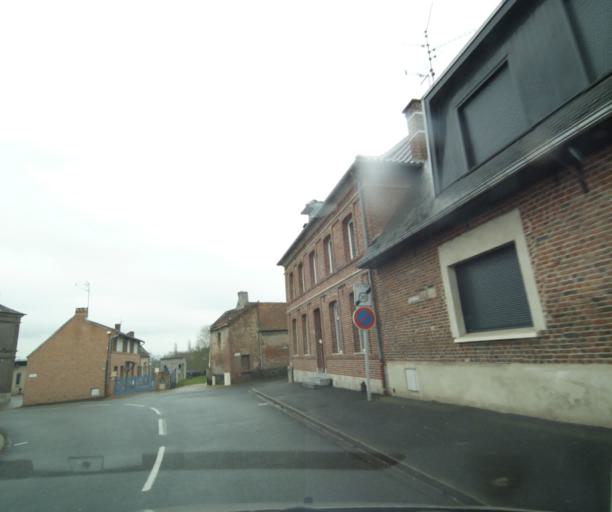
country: FR
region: Nord-Pas-de-Calais
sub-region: Departement du Nord
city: Prouvy
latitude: 50.3177
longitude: 3.4499
